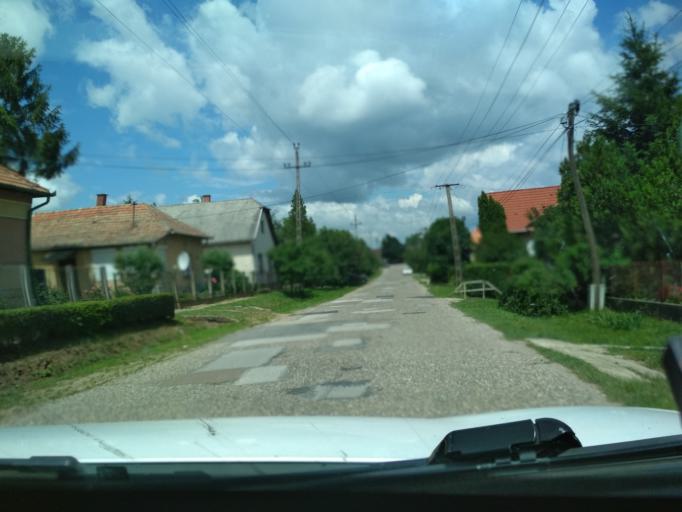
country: HU
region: Jasz-Nagykun-Szolnok
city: Tiszafured
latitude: 47.6110
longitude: 20.7715
